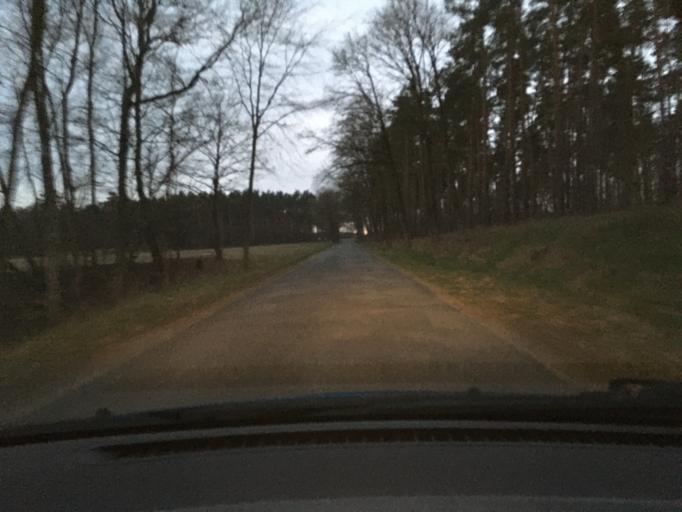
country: DE
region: Lower Saxony
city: Neetze
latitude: 53.2454
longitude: 10.6260
